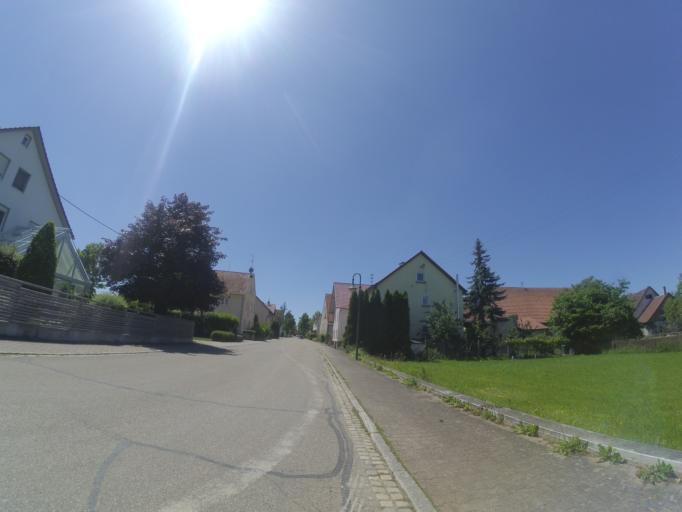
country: DE
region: Baden-Wuerttemberg
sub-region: Tuebingen Region
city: Blaubeuren
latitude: 48.4634
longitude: 9.8452
